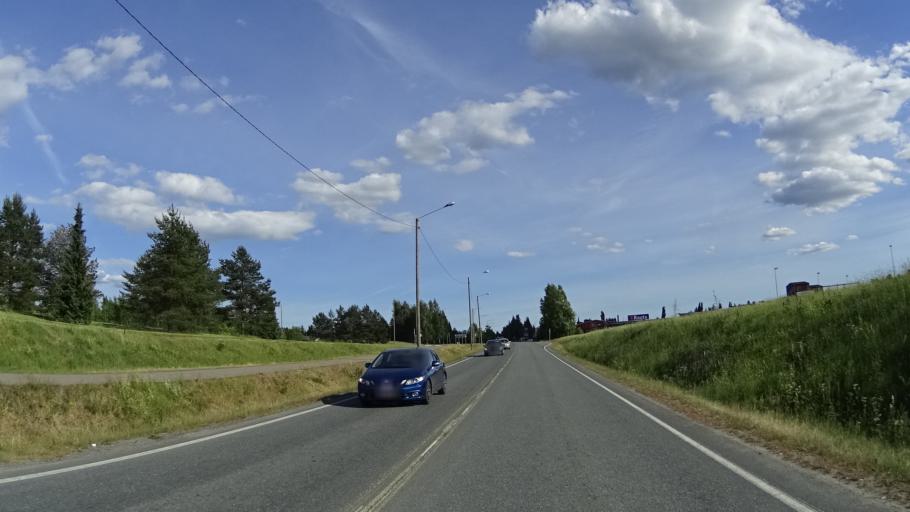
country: FI
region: Haeme
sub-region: Forssa
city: Forssa
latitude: 60.8271
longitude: 23.6240
